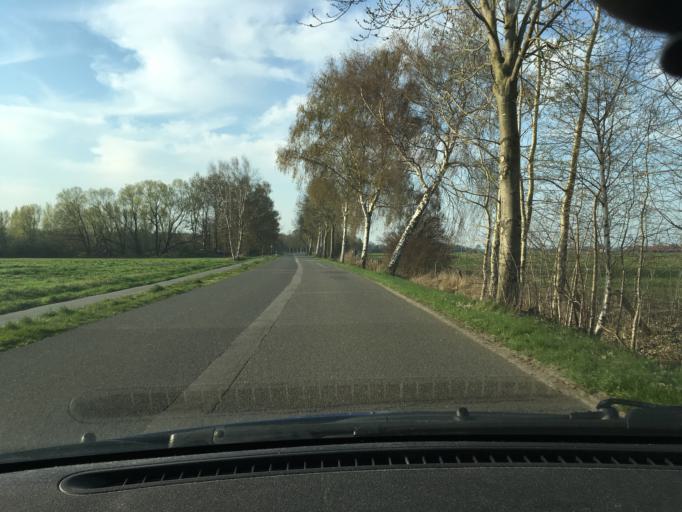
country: DE
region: Lower Saxony
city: Stelle
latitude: 53.4166
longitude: 10.0599
